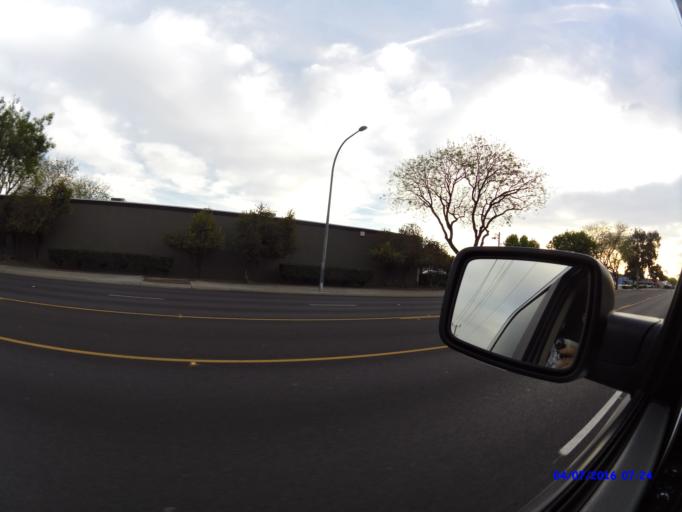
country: US
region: California
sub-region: Stanislaus County
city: Bystrom
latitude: 37.6381
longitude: -120.9593
